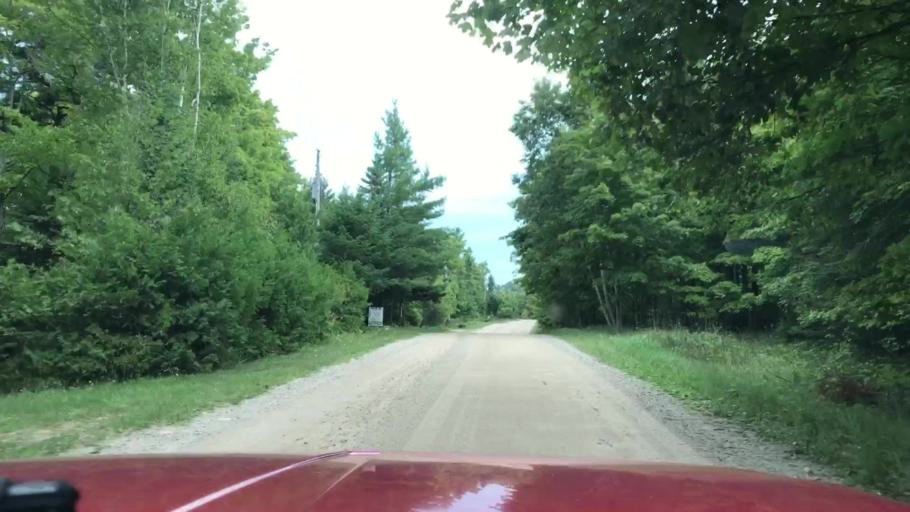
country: US
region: Michigan
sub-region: Charlevoix County
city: Charlevoix
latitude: 45.7302
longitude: -85.5648
